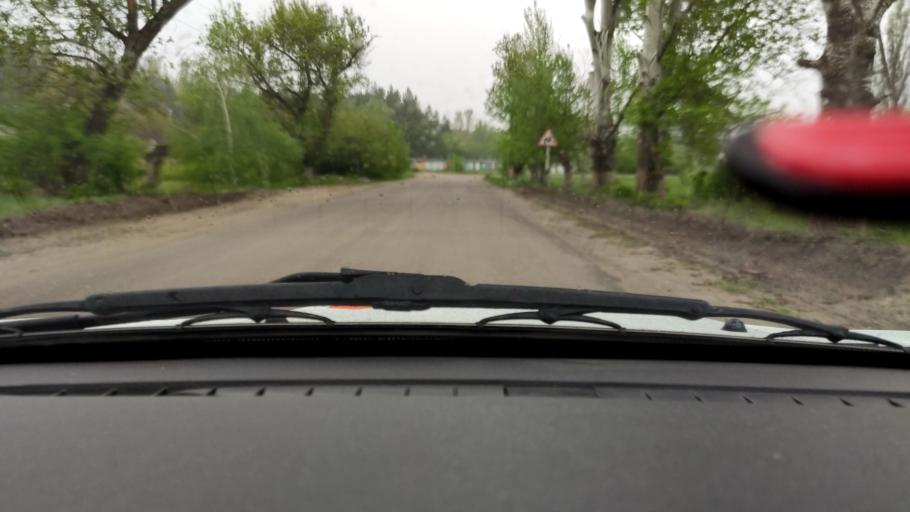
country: RU
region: Voronezj
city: Strelitsa
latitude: 51.6083
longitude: 38.8986
